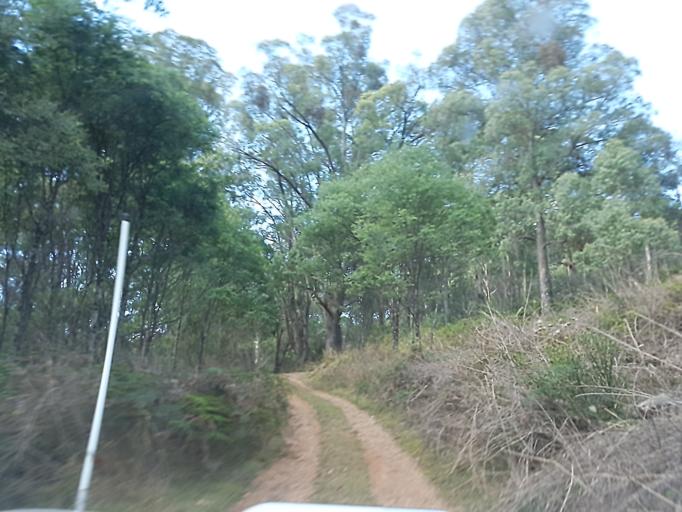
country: AU
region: Victoria
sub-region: Alpine
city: Mount Beauty
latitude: -36.9100
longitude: 147.0492
